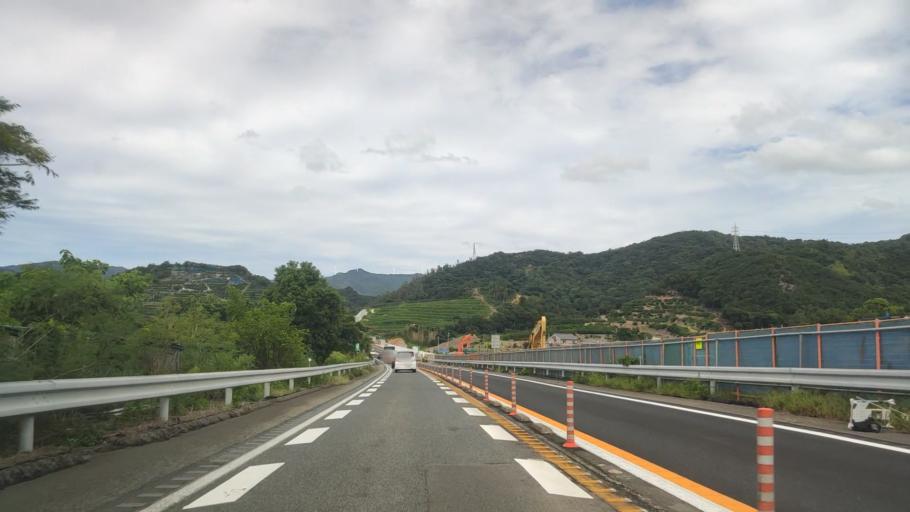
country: JP
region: Wakayama
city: Gobo
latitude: 33.9126
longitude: 135.1944
